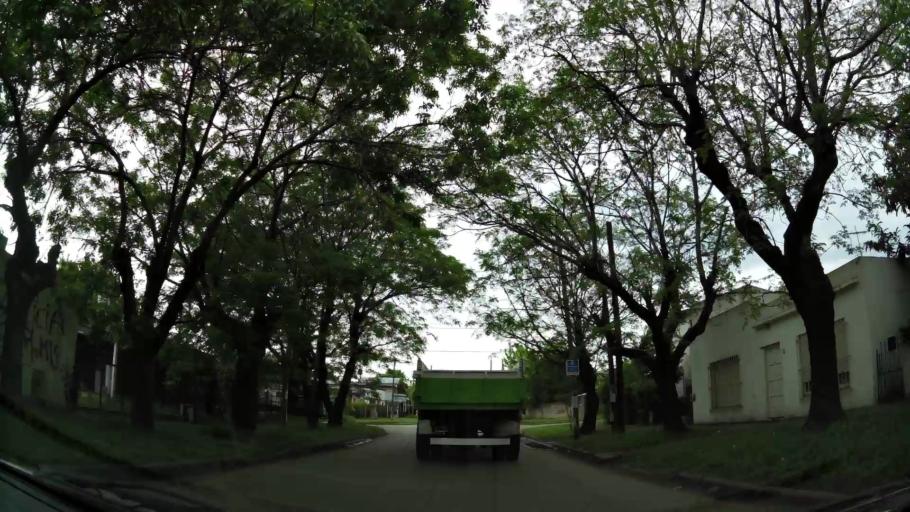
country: AR
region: Buenos Aires
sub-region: Partido de Quilmes
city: Quilmes
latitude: -34.8002
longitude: -58.2733
